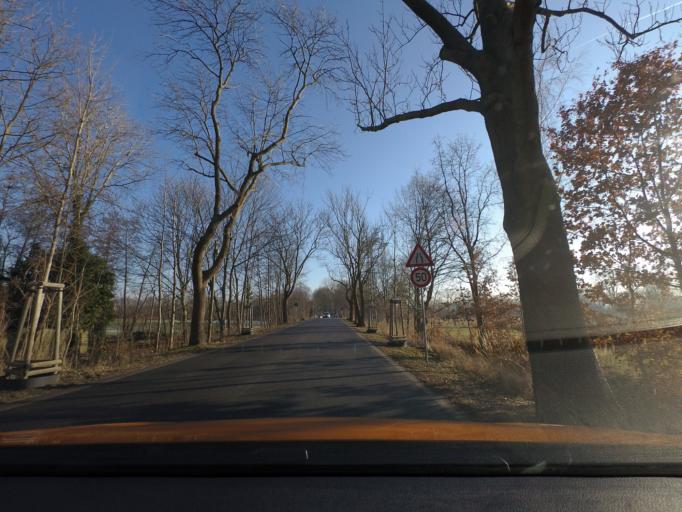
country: DE
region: Brandenburg
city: Werder
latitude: 52.4547
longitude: 12.9699
